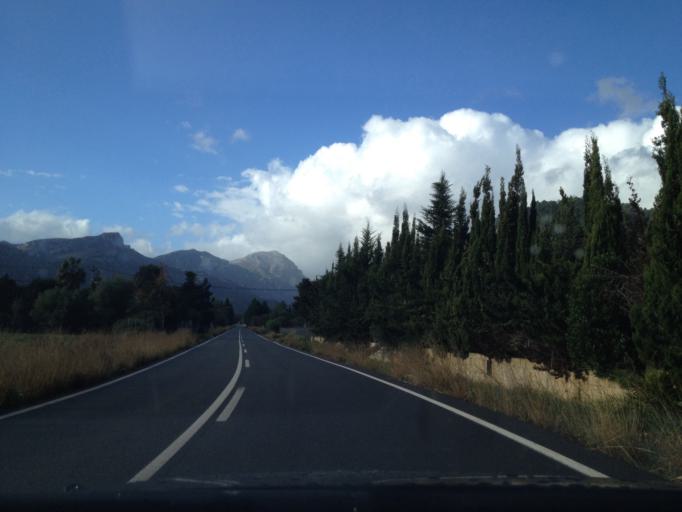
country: ES
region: Balearic Islands
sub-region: Illes Balears
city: Pollenca
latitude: 39.8830
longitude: 3.0086
